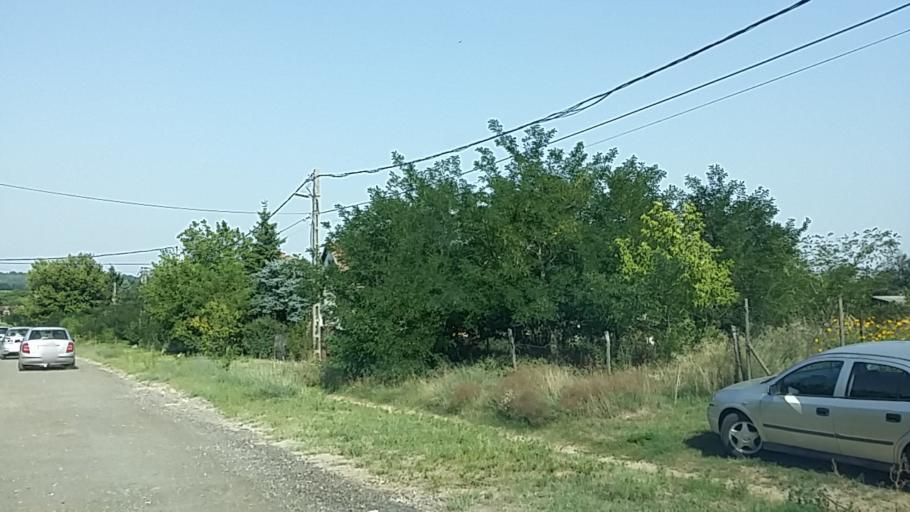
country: HU
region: Pest
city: Erdokertes
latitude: 47.6643
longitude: 19.3335
